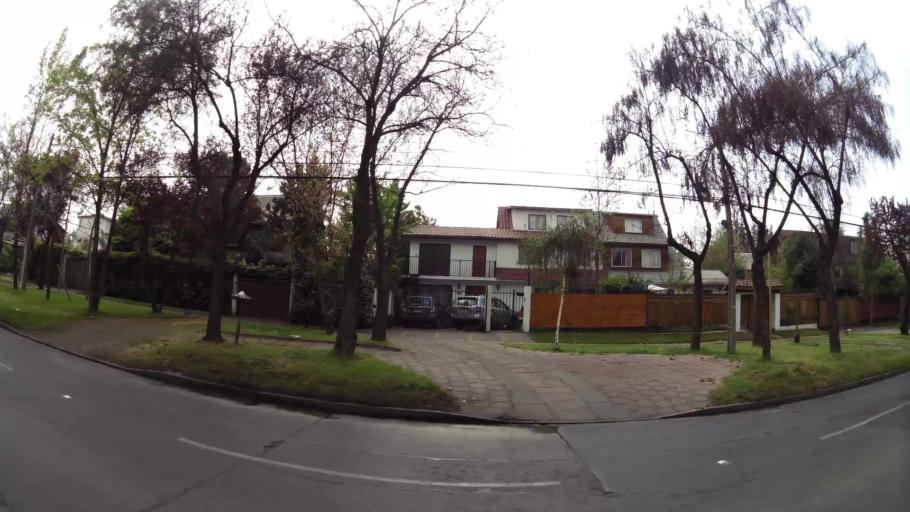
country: CL
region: Santiago Metropolitan
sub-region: Provincia de Santiago
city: Villa Presidente Frei, Nunoa, Santiago, Chile
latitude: -33.4120
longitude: -70.5411
